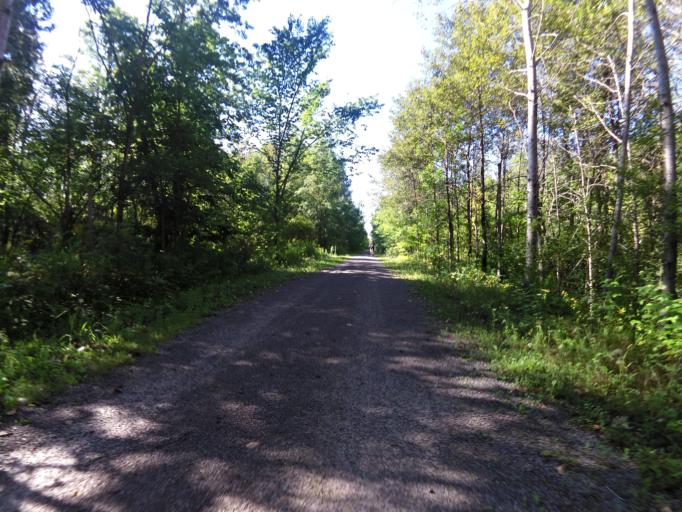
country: CA
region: Ontario
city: Ottawa
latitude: 45.2218
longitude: -75.6218
